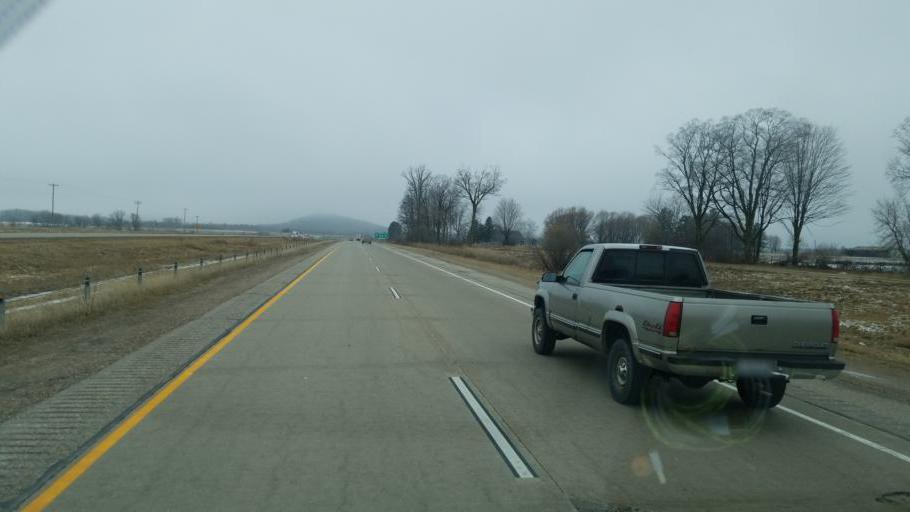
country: US
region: Wisconsin
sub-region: Waupaca County
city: Waupaca
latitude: 44.3295
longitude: -89.0304
